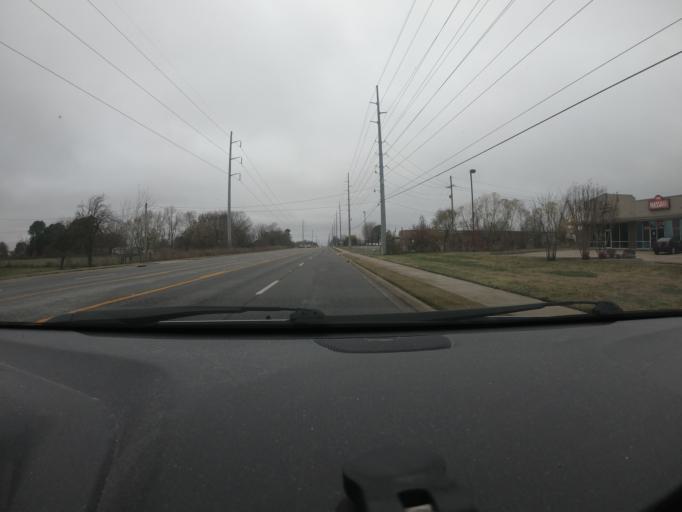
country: US
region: Arkansas
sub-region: Benton County
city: Bentonville
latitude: 36.3573
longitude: -94.2242
